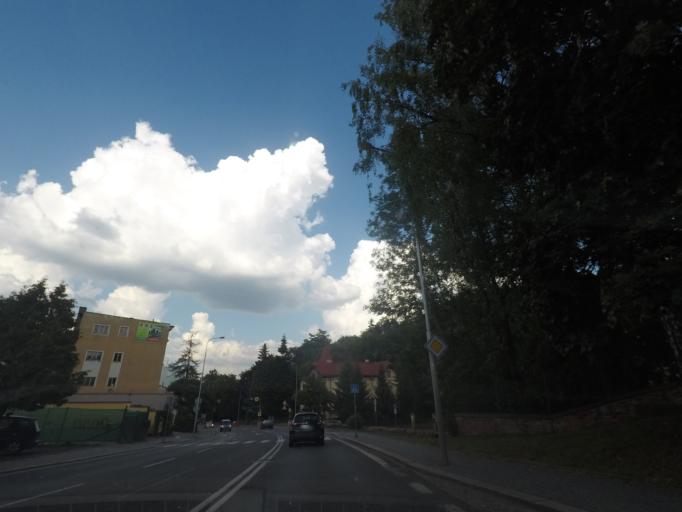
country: CZ
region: Kralovehradecky
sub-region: Okres Trutnov
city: Trutnov
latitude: 50.5594
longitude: 15.9120
